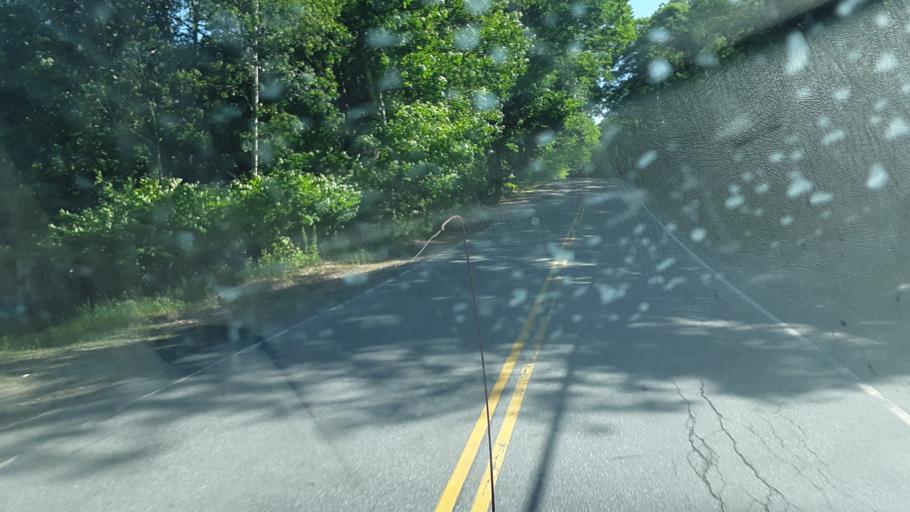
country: US
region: New Hampshire
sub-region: Grafton County
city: North Haverhill
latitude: 44.0964
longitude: -71.9412
